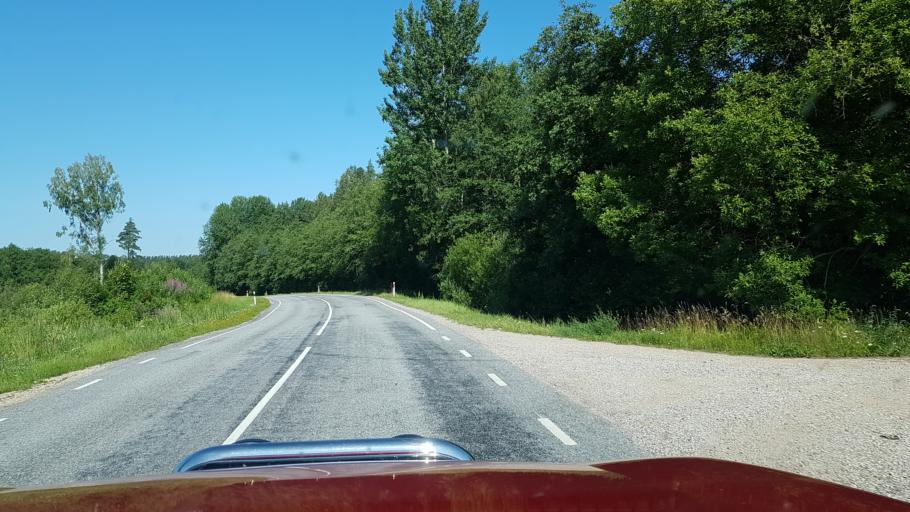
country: EE
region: Polvamaa
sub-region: Polva linn
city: Polva
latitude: 58.0860
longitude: 26.8316
